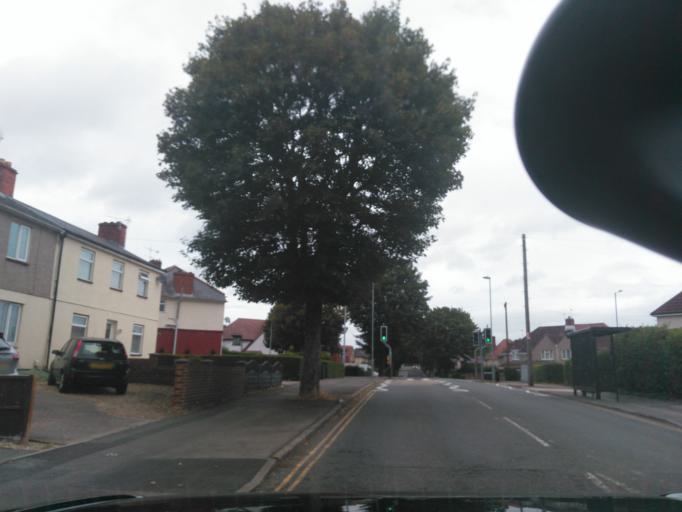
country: GB
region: England
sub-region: Borough of Swindon
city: Swindon
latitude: 51.5796
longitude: -1.7835
